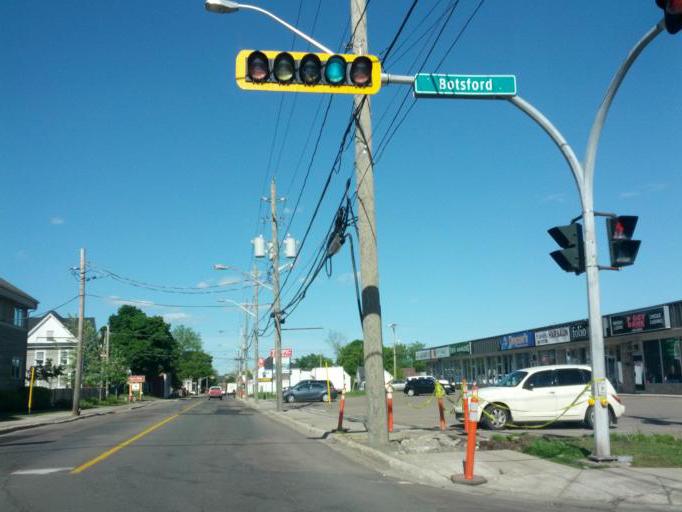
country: CA
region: New Brunswick
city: Moncton
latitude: 46.0923
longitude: -64.7774
